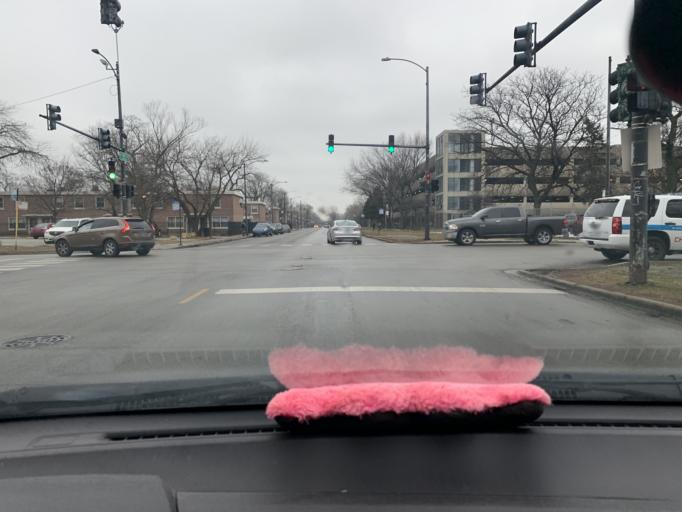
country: US
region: Illinois
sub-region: Cook County
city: Chicago
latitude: 41.8447
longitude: -87.6949
